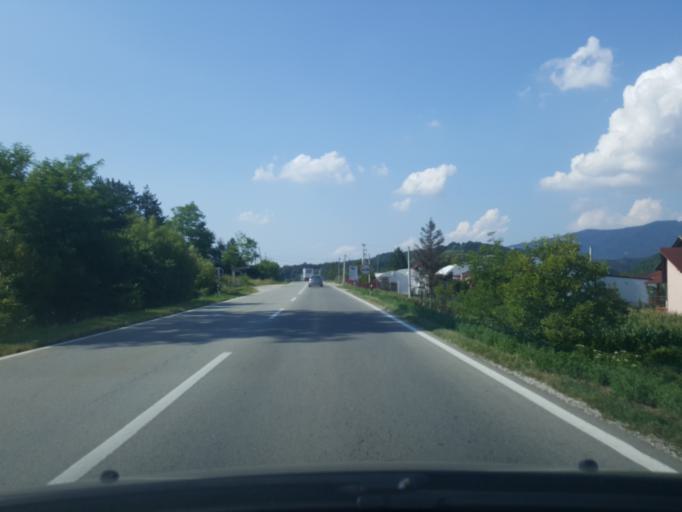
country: RS
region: Central Serbia
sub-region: Moravicki Okrug
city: Gornji Milanovac
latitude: 44.0668
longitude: 20.4911
